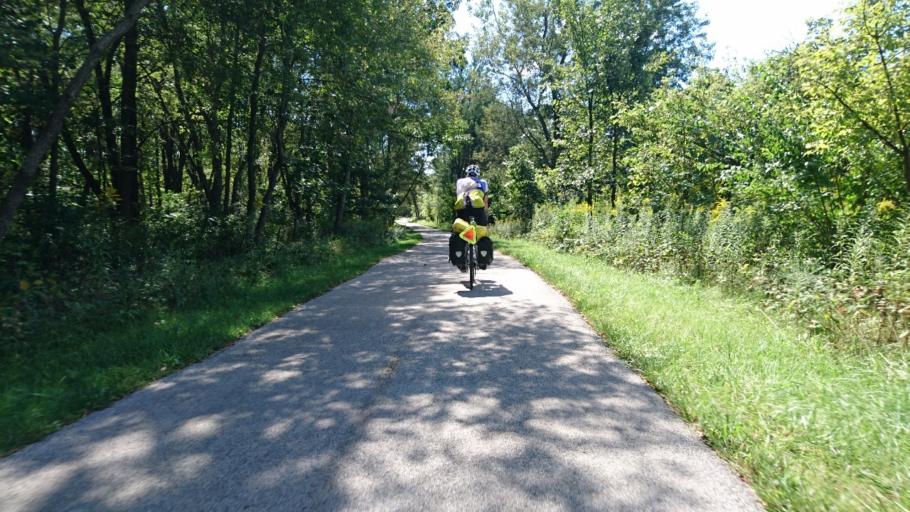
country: US
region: Illinois
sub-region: Cook County
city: Lansing
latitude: 41.5477
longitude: -87.5584
